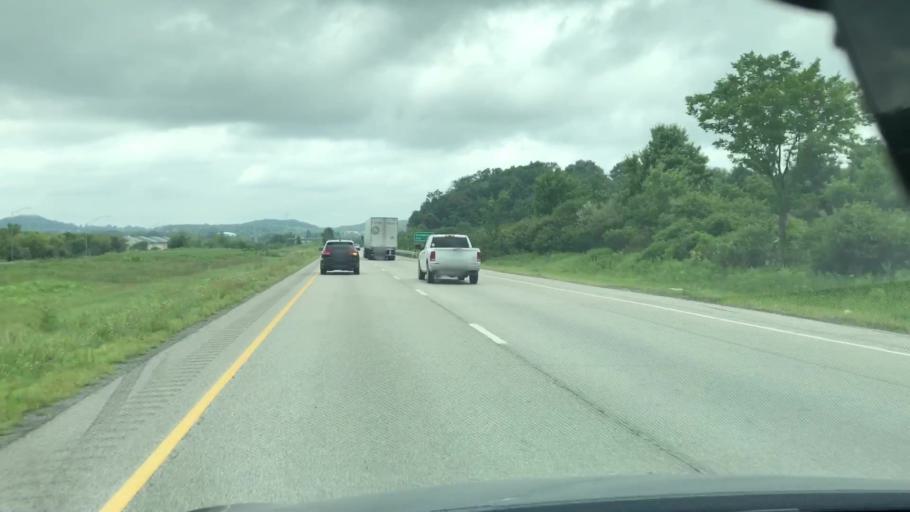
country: US
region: Pennsylvania
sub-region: Butler County
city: Cranberry Township
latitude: 40.6937
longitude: -80.0980
